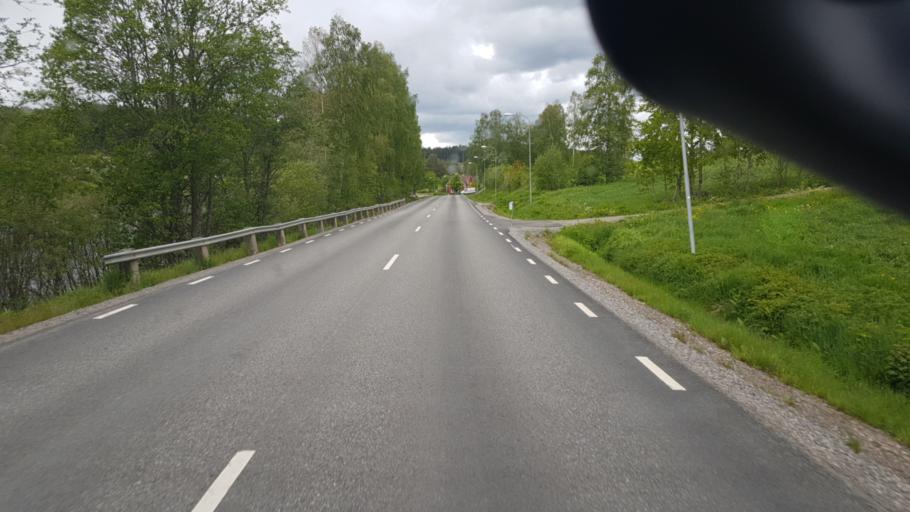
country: SE
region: Vaermland
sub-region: Eda Kommun
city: Amotfors
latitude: 59.8834
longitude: 12.5264
